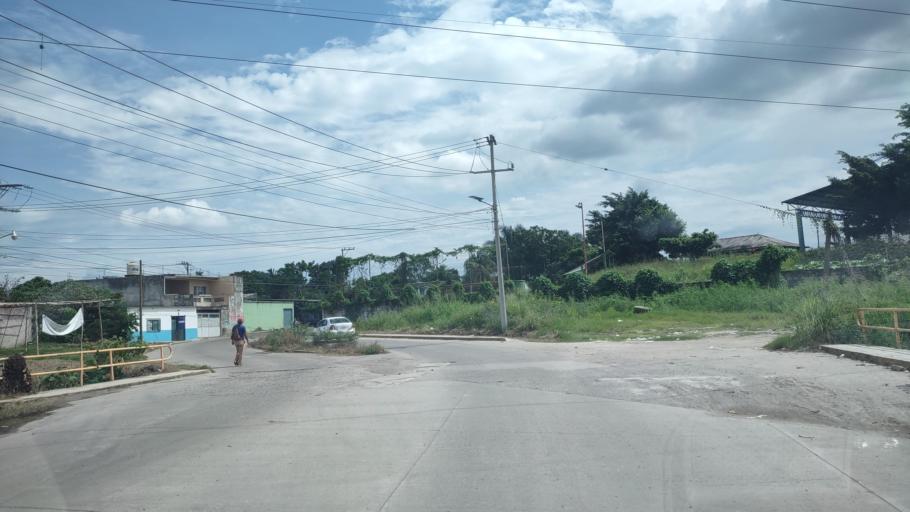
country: MX
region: Veracruz
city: Martinez de la Torre
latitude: 20.0709
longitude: -97.0748
